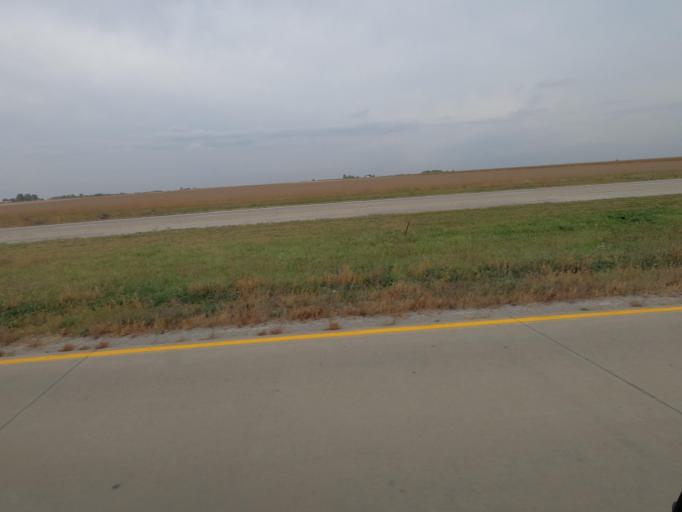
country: US
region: Iowa
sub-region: Marion County
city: Pella
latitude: 41.3694
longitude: -92.7974
